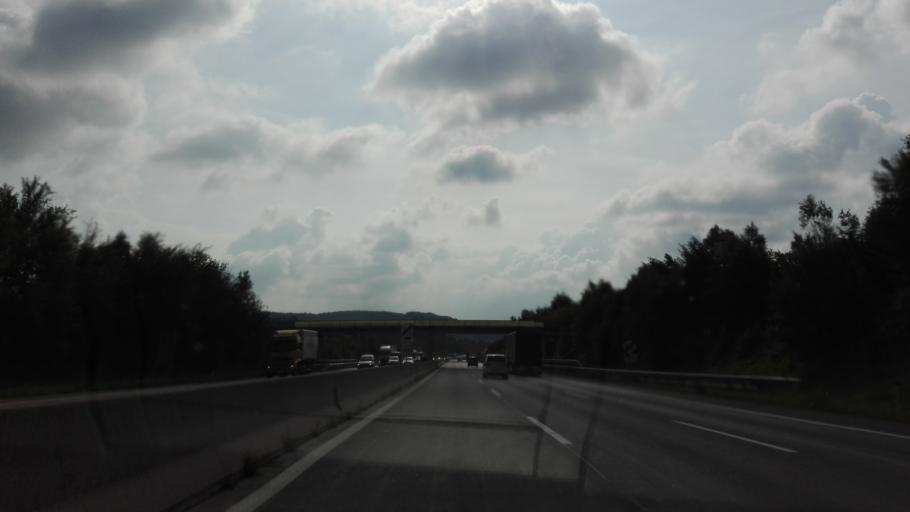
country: AT
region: Lower Austria
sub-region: Politischer Bezirk Melk
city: Blindenmarkt
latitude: 48.1373
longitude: 14.9687
